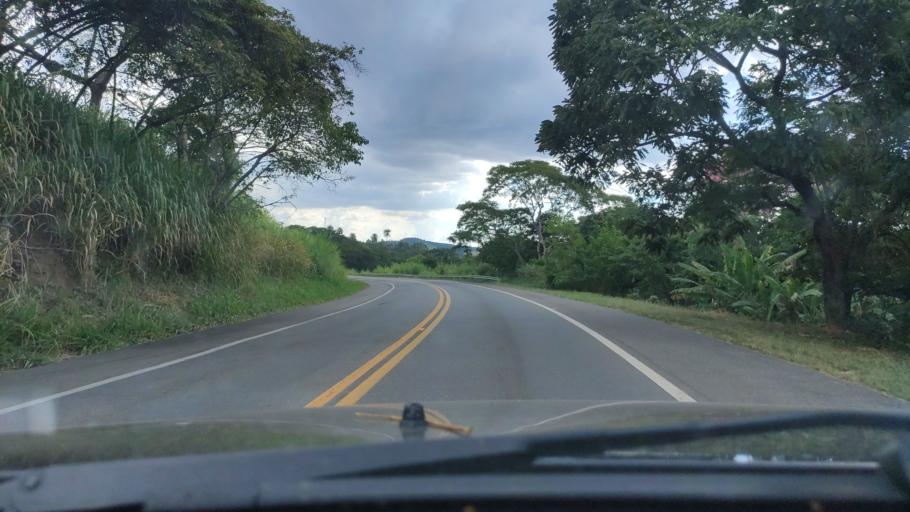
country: BR
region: Sao Paulo
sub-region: Aguas De Lindoia
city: Aguas de Lindoia
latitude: -22.4604
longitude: -46.7245
